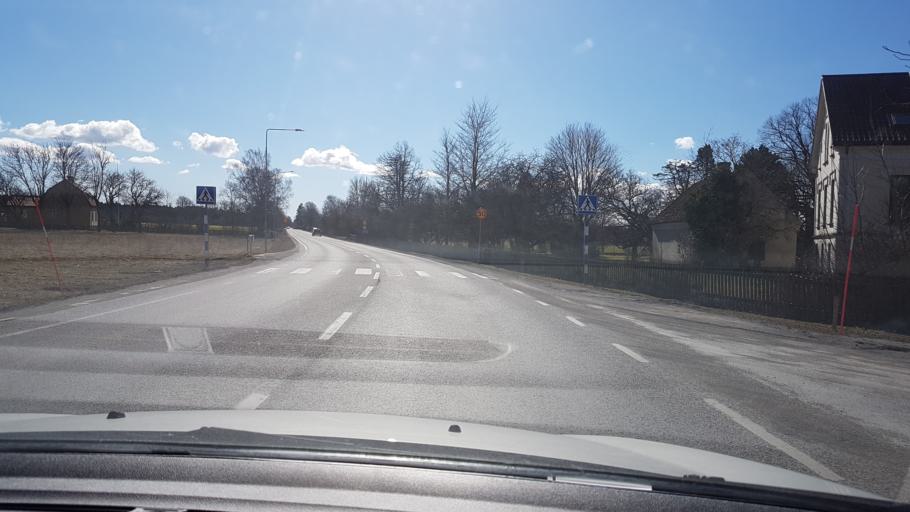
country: SE
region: Gotland
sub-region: Gotland
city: Visby
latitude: 57.5271
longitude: 18.4403
